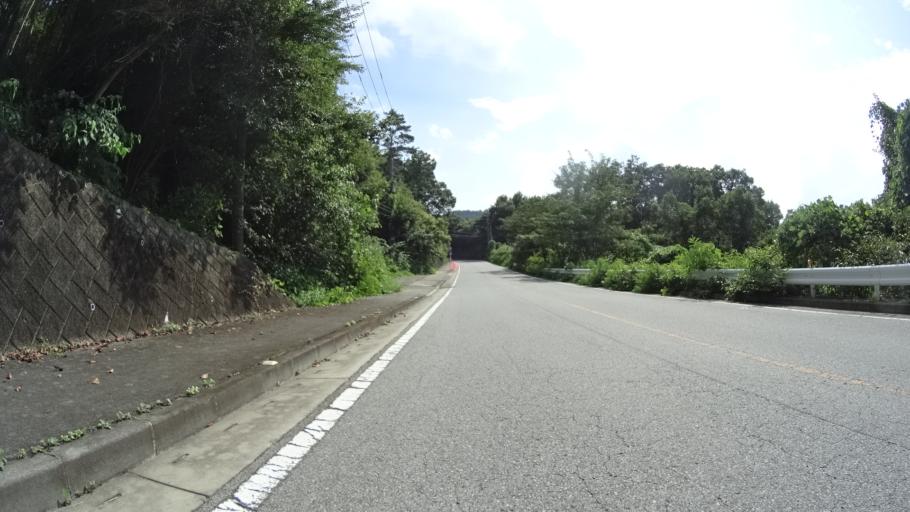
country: JP
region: Yamanashi
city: Kofu-shi
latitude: 35.7105
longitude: 138.5537
